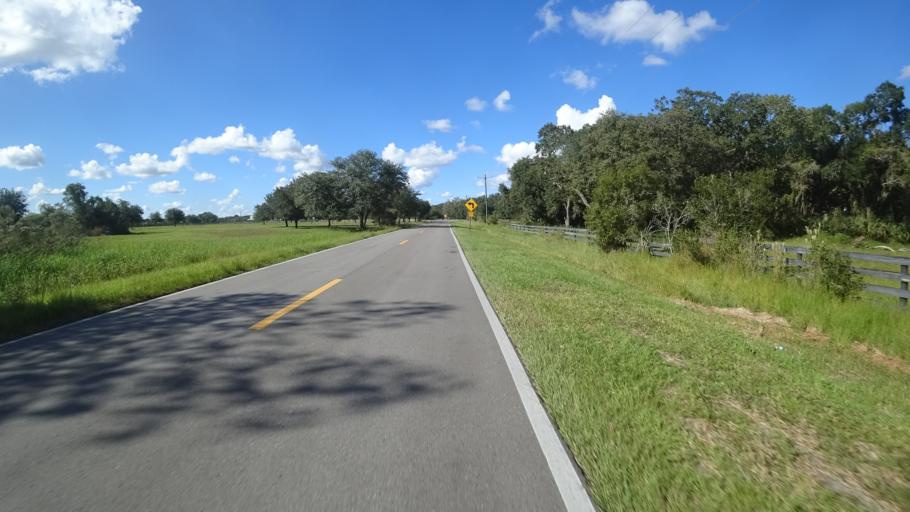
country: US
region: Florida
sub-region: Sarasota County
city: Lake Sarasota
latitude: 27.2873
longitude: -82.2168
